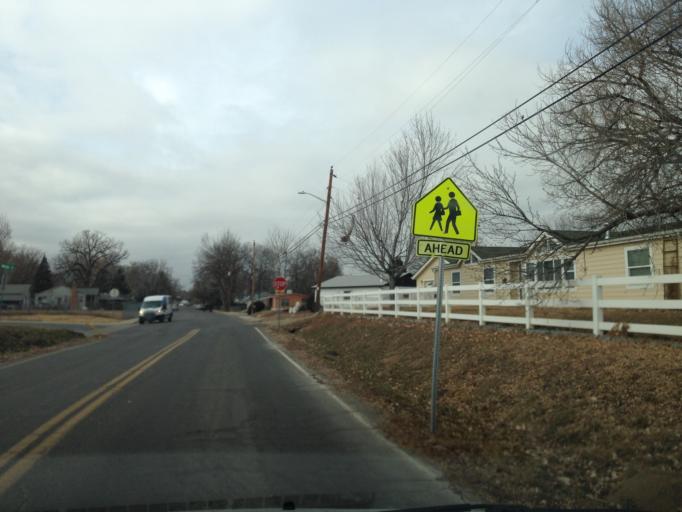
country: US
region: Colorado
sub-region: Boulder County
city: Lafayette
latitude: 39.9941
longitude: -105.0805
